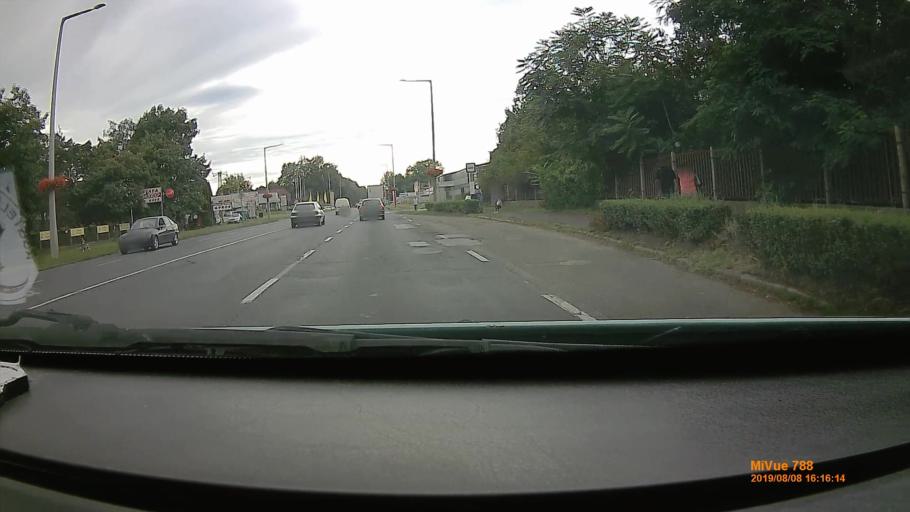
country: HU
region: Szabolcs-Szatmar-Bereg
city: Mateszalka
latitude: 47.9613
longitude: 22.3065
